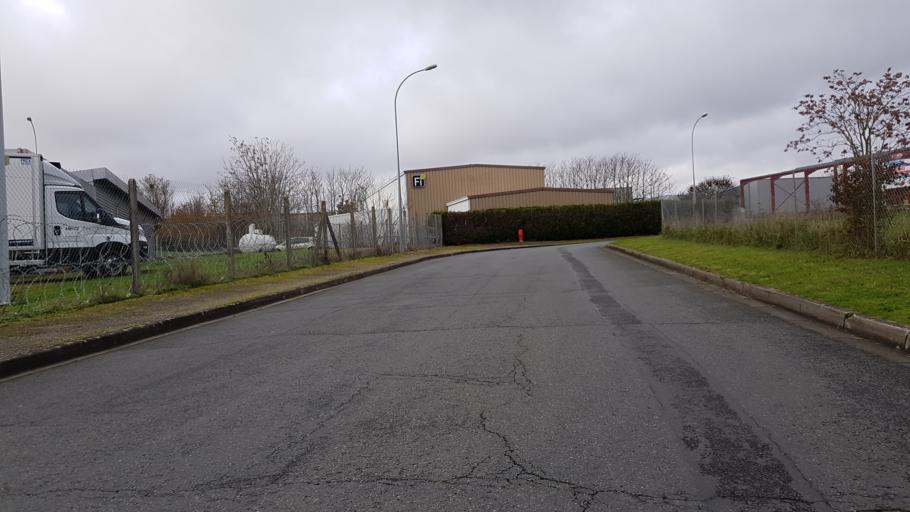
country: FR
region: Poitou-Charentes
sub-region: Departement de la Vienne
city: Chasseneuil-du-Poitou
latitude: 46.6561
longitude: 0.3719
